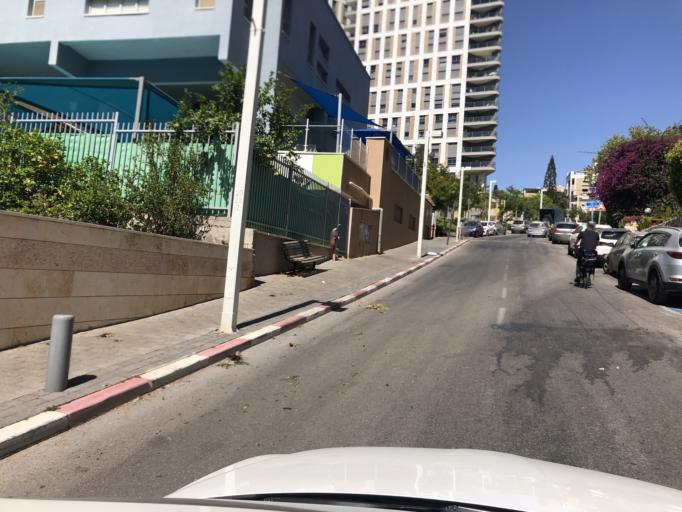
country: IL
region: Tel Aviv
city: Ramat Gan
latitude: 32.0783
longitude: 34.8098
